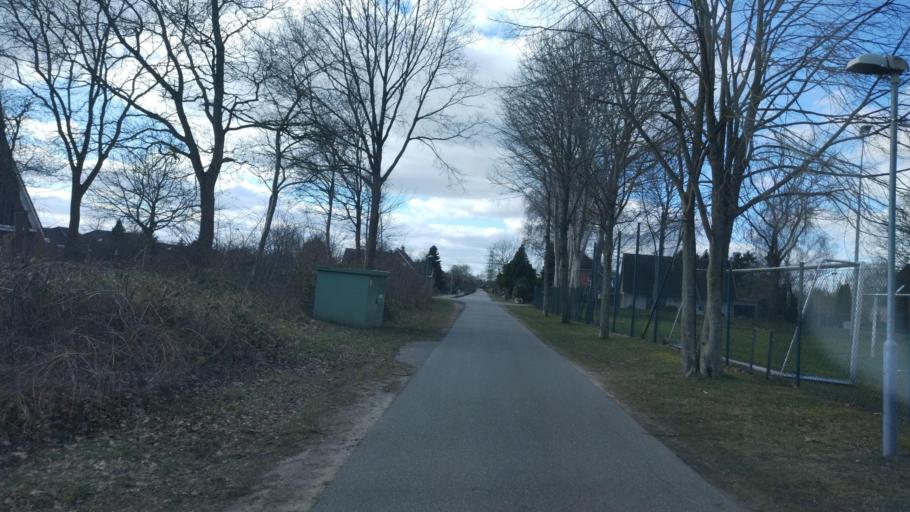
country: DE
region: Schleswig-Holstein
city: Gross Rheide
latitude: 54.4407
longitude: 9.4335
